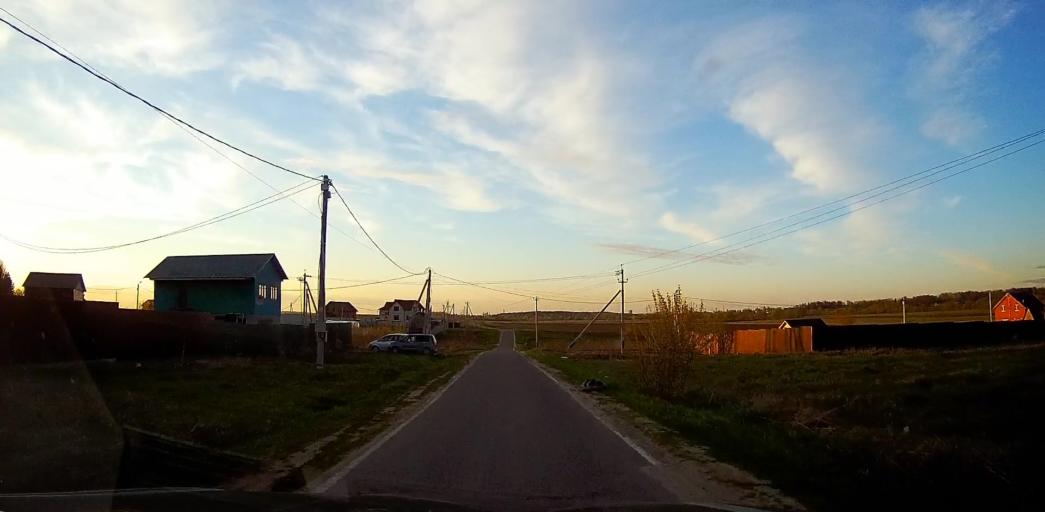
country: RU
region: Moskovskaya
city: Peski
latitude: 55.2127
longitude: 38.7396
